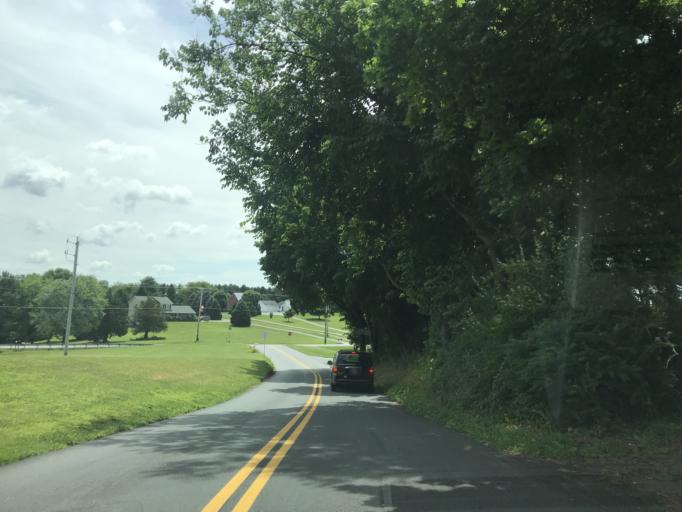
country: US
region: Maryland
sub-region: Carroll County
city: Hampstead
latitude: 39.6281
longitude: -76.7958
